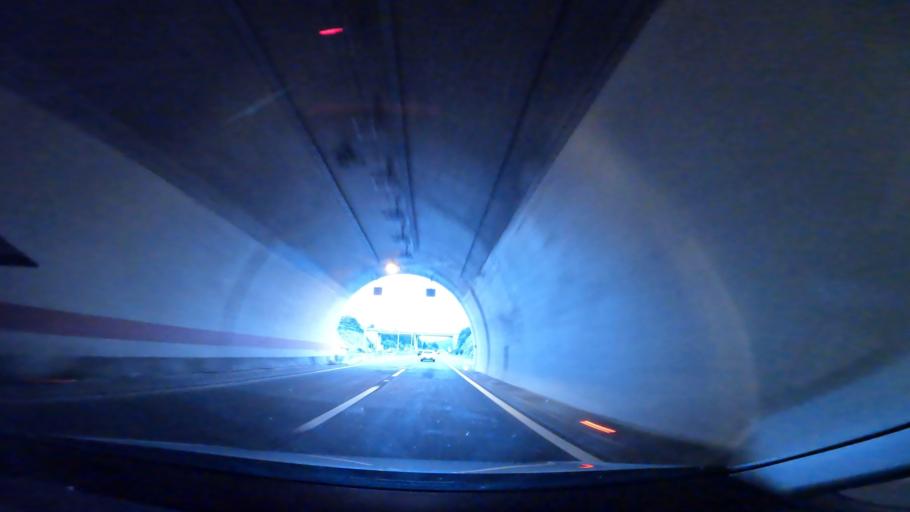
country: HR
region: Primorsko-Goranska
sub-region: Grad Delnice
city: Delnice
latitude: 45.3694
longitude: 14.7633
